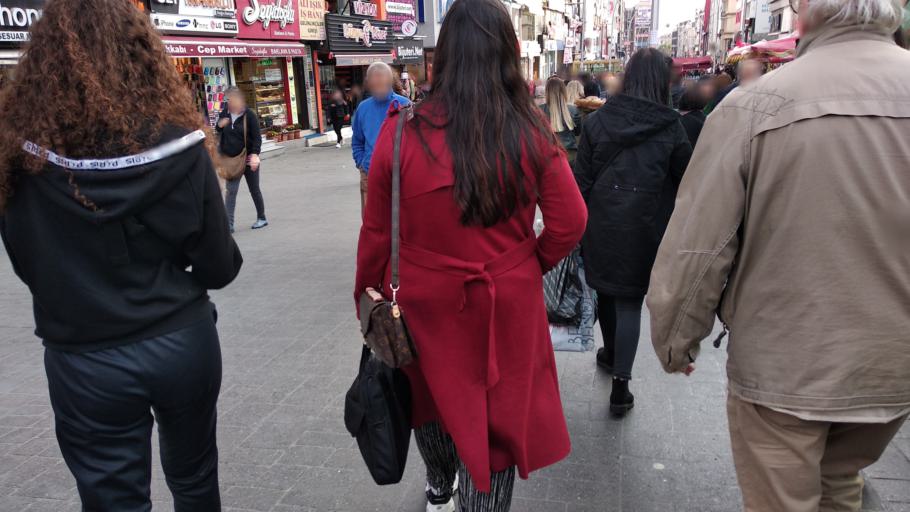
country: TR
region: Istanbul
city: Bahcelievler
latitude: 40.9803
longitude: 28.8740
